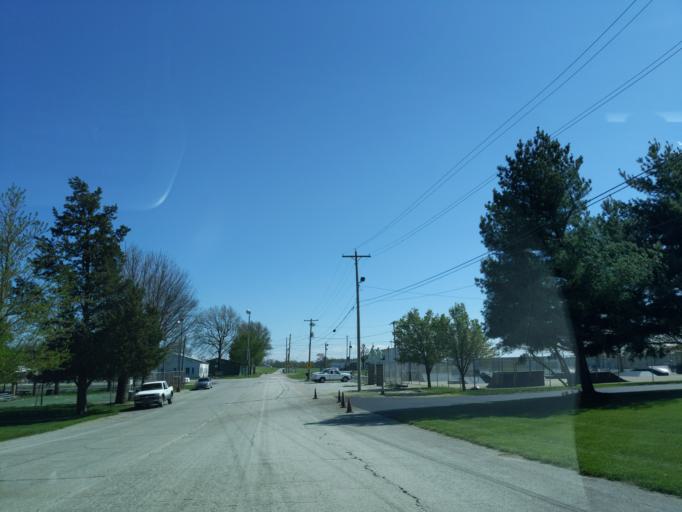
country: US
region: Indiana
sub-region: Decatur County
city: Greensburg
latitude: 39.3299
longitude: -85.5183
